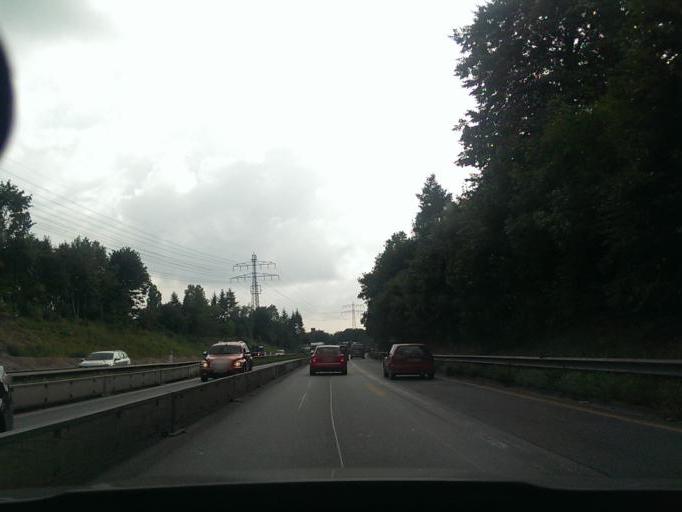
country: DE
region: Hamburg
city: Eidelstedt
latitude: 53.6278
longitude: 9.9212
